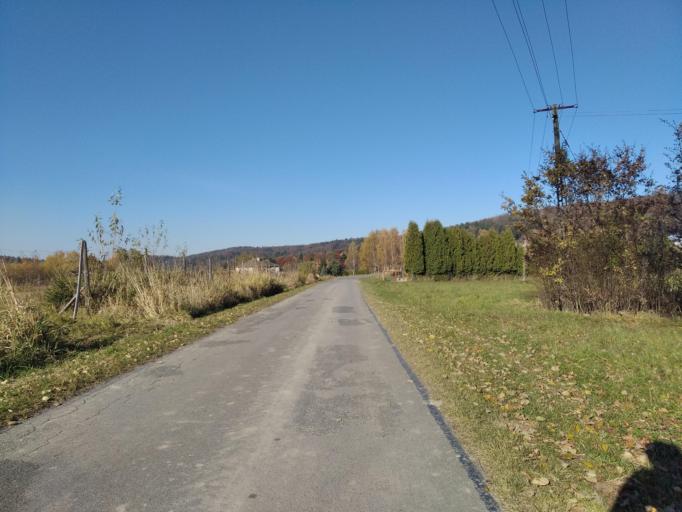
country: PL
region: Subcarpathian Voivodeship
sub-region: Powiat strzyzowski
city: Frysztak
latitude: 49.8510
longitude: 21.5933
